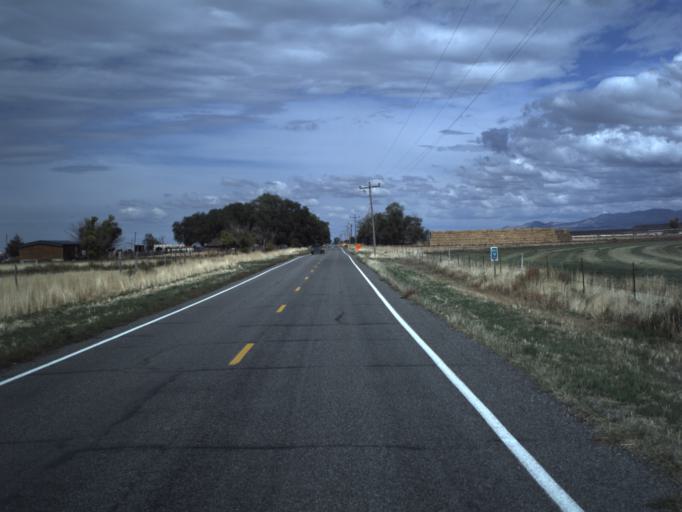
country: US
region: Utah
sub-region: Millard County
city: Fillmore
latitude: 39.0413
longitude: -112.4098
